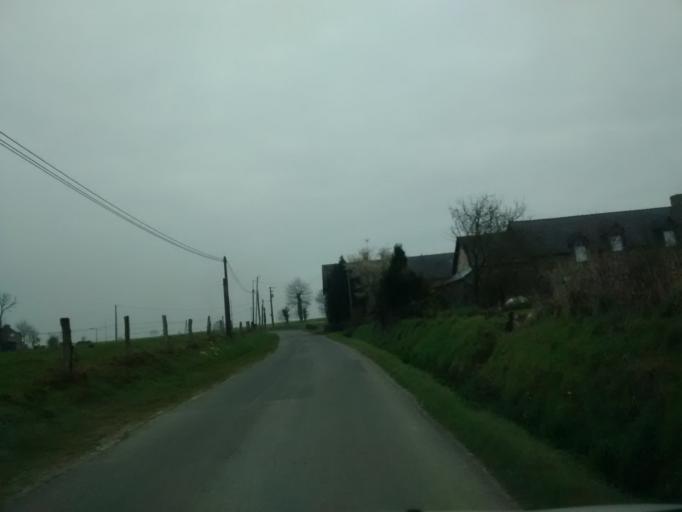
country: FR
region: Brittany
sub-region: Departement d'Ille-et-Vilaine
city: Sens-de-Bretagne
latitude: 48.3893
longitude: -1.5258
